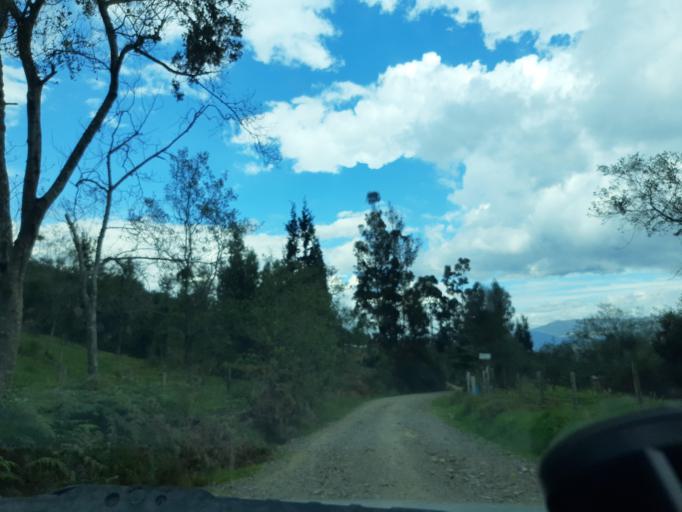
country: CO
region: Boyaca
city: Raquira
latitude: 5.5079
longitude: -73.6834
